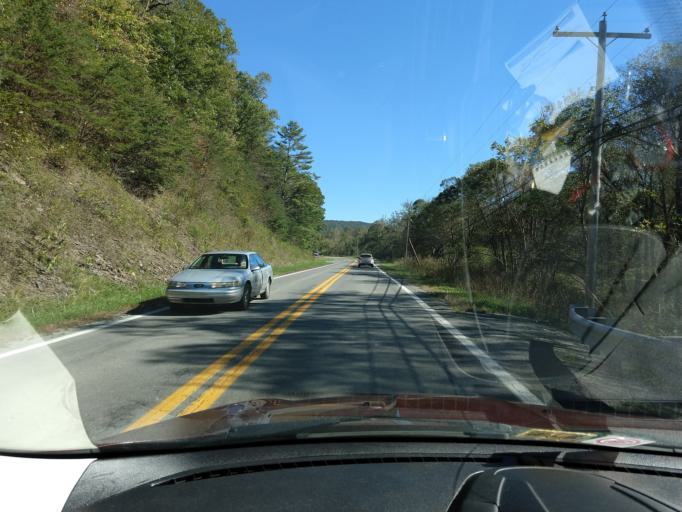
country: US
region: West Virginia
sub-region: Pocahontas County
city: Marlinton
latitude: 38.2004
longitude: -80.0356
